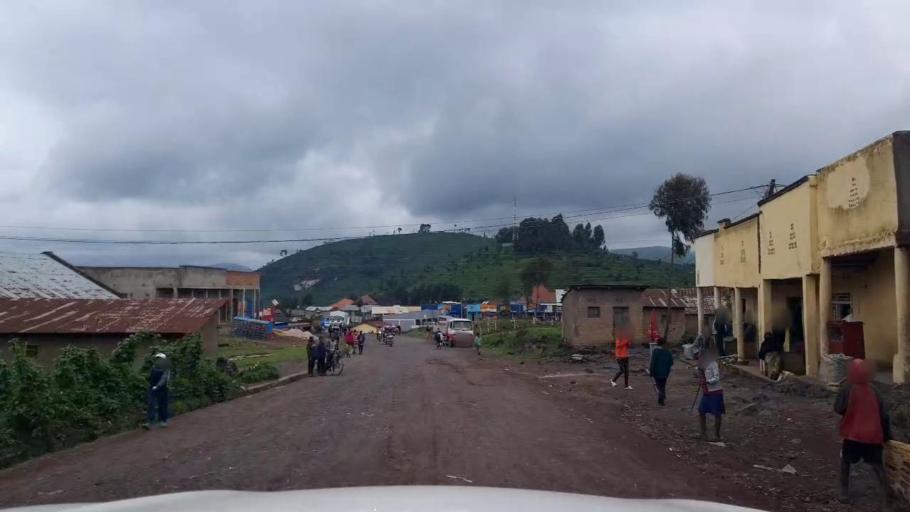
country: RW
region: Northern Province
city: Musanze
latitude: -1.6097
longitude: 29.4520
